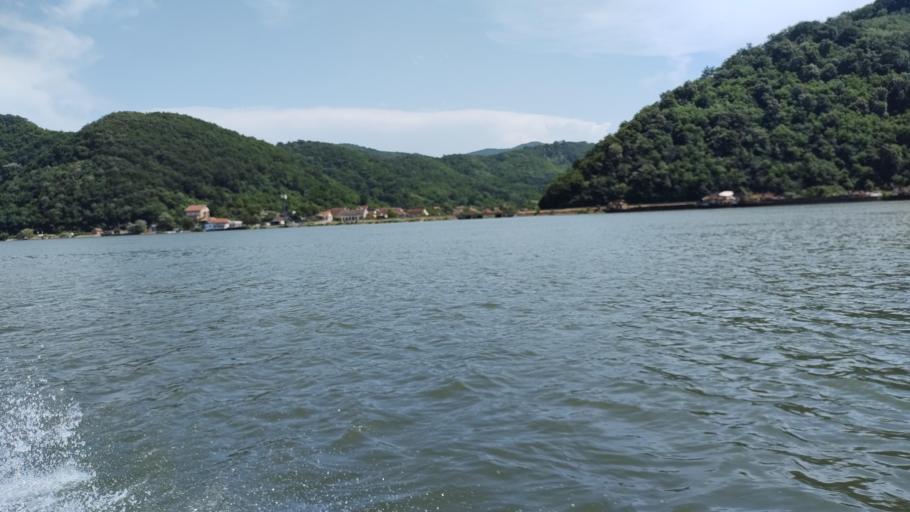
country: RS
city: Radenka
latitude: 44.6595
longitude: 21.7619
